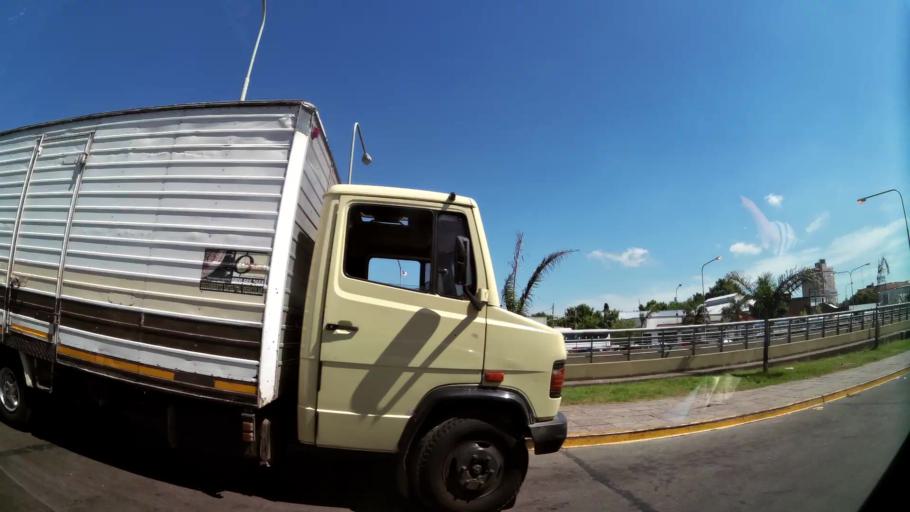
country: AR
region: Buenos Aires
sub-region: Partido de Tigre
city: Tigre
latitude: -34.4363
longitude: -58.5681
